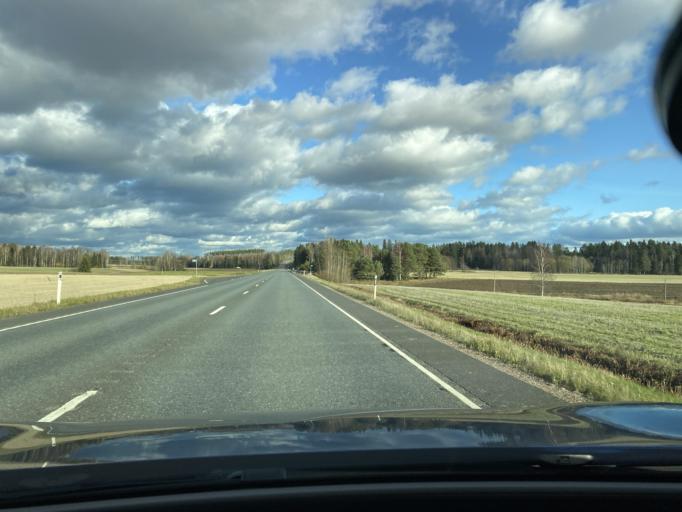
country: FI
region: Haeme
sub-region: Riihimaeki
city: Hausjaervi
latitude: 60.7868
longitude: 24.9302
